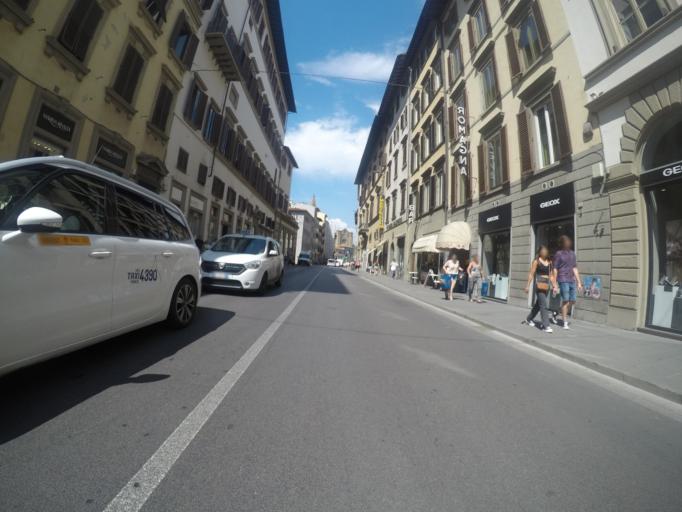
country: IT
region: Tuscany
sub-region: Province of Florence
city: Florence
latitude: 43.7735
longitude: 11.2520
